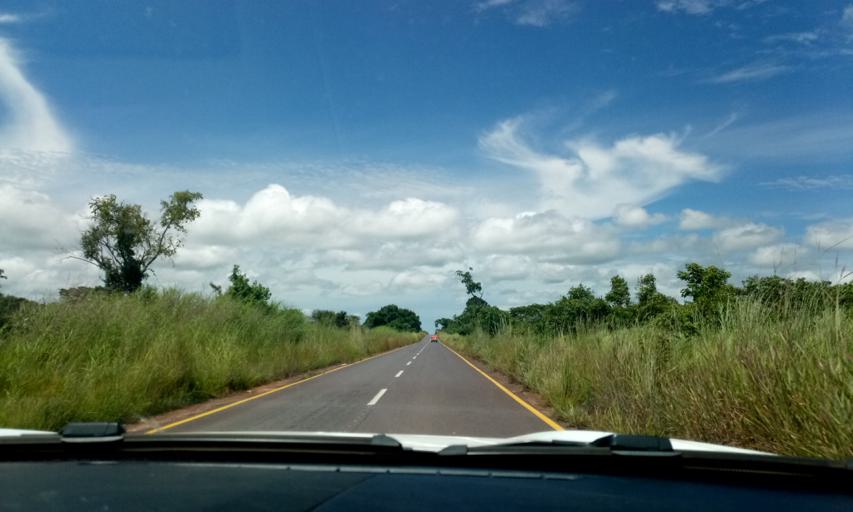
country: CD
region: Katanga
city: Lubumbashi
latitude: -11.1091
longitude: 27.9712
